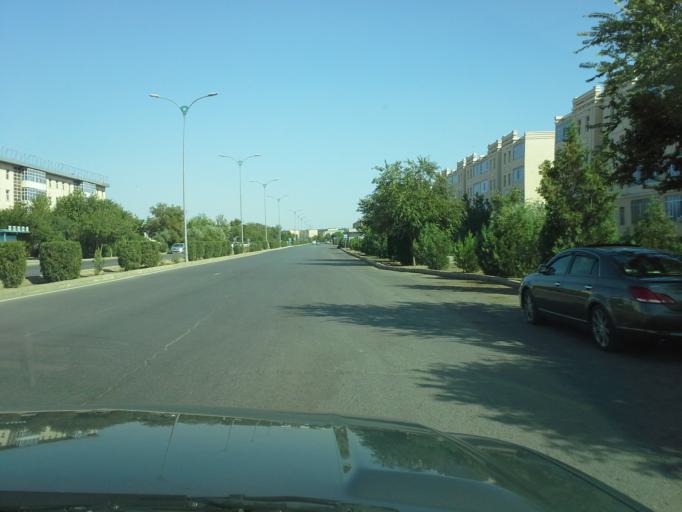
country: TM
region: Dasoguz
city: Dasoguz
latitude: 41.8239
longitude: 59.9647
